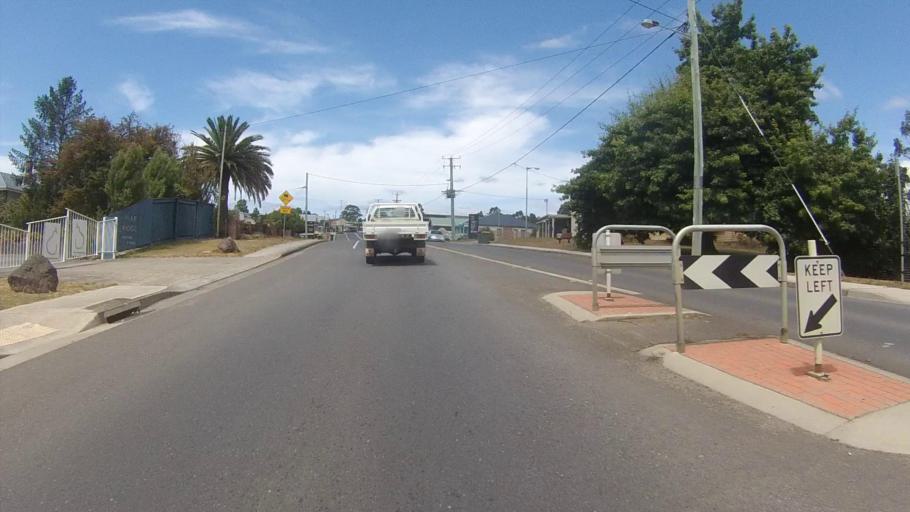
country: AU
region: Tasmania
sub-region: Kingborough
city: Margate
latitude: -43.0235
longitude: 147.2598
